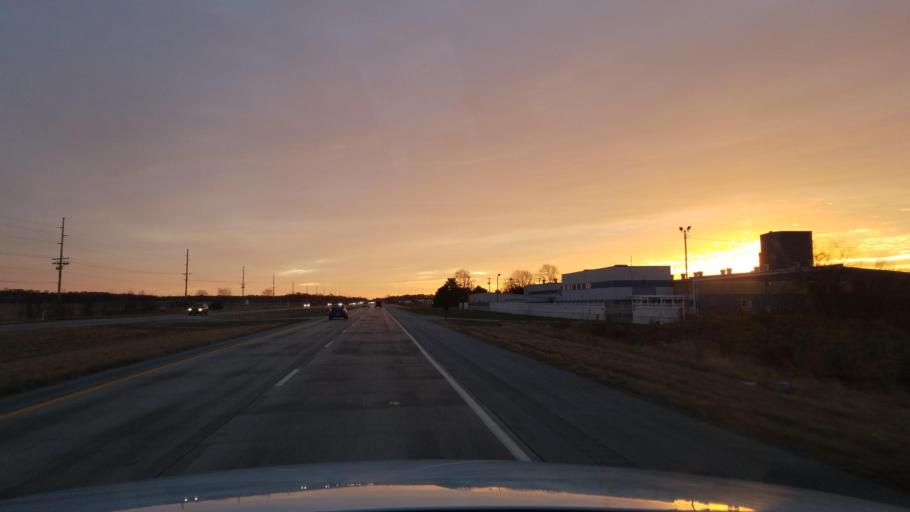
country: US
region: Indiana
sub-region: Posey County
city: Mount Vernon
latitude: 37.9421
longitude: -87.7860
